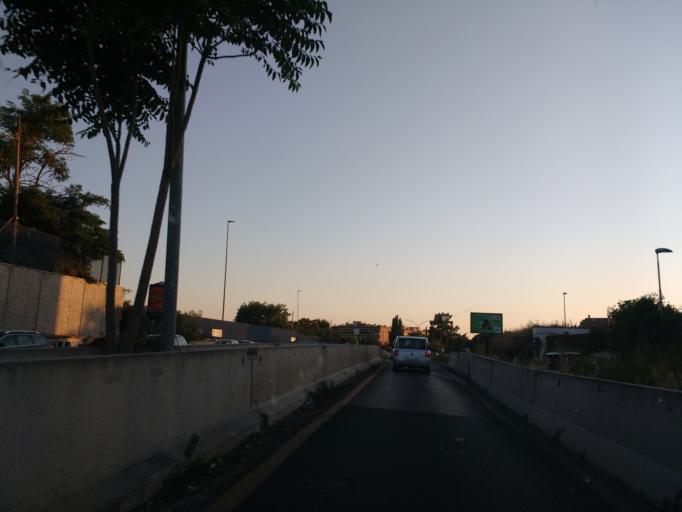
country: IT
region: Latium
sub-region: Citta metropolitana di Roma Capitale
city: Setteville
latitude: 41.9397
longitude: 12.6299
